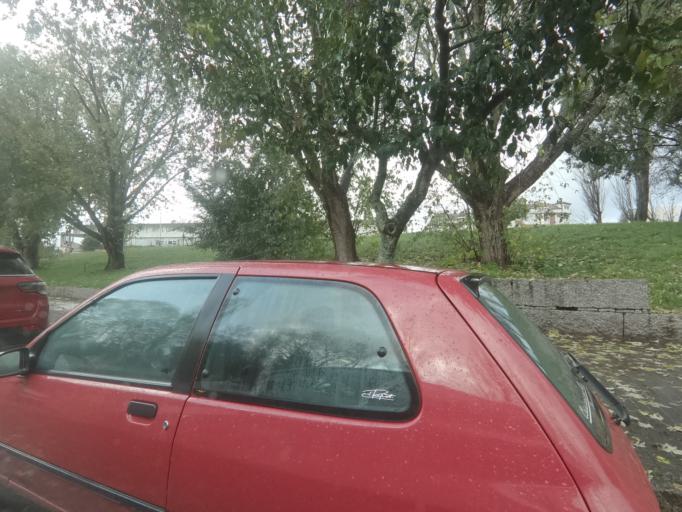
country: ES
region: Galicia
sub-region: Provincia de Pontevedra
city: Pontevedra
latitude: 42.4386
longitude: -8.6391
